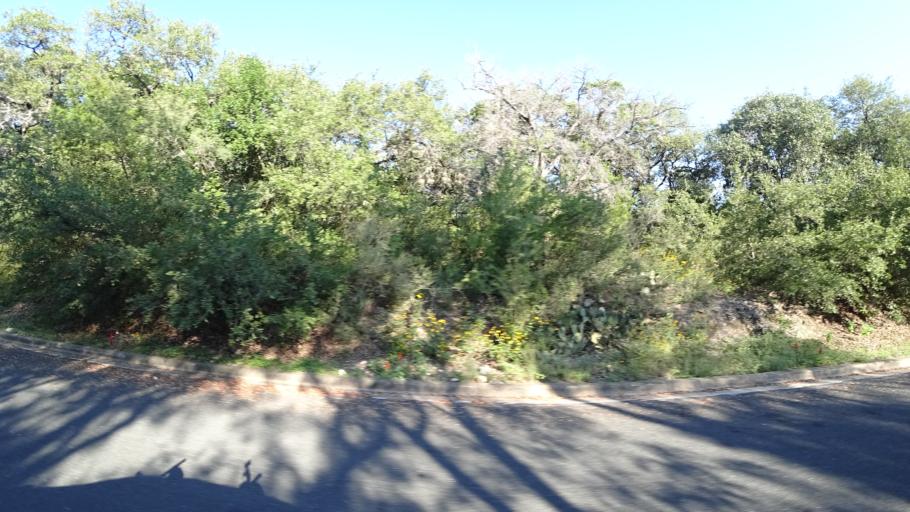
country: US
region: Texas
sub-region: Travis County
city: Rollingwood
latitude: 30.2639
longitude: -97.7957
